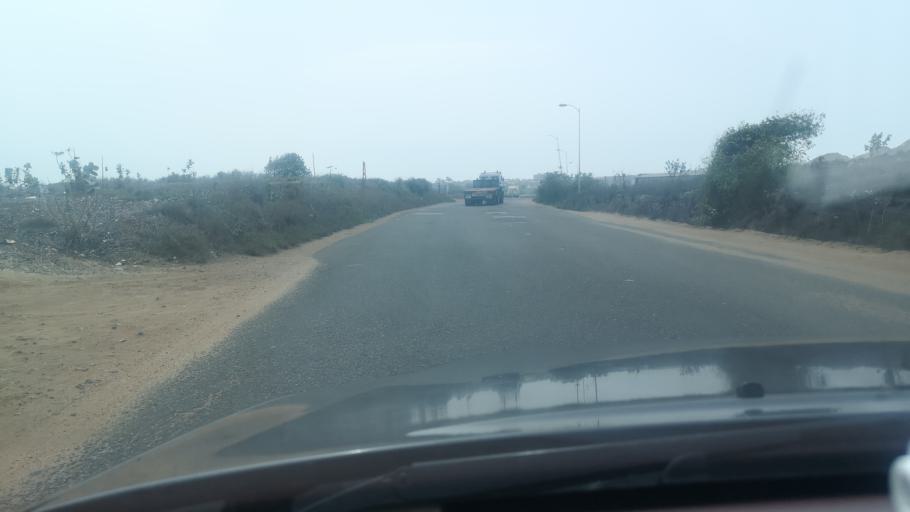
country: GH
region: Greater Accra
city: Nungua
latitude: 5.6103
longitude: -0.0517
